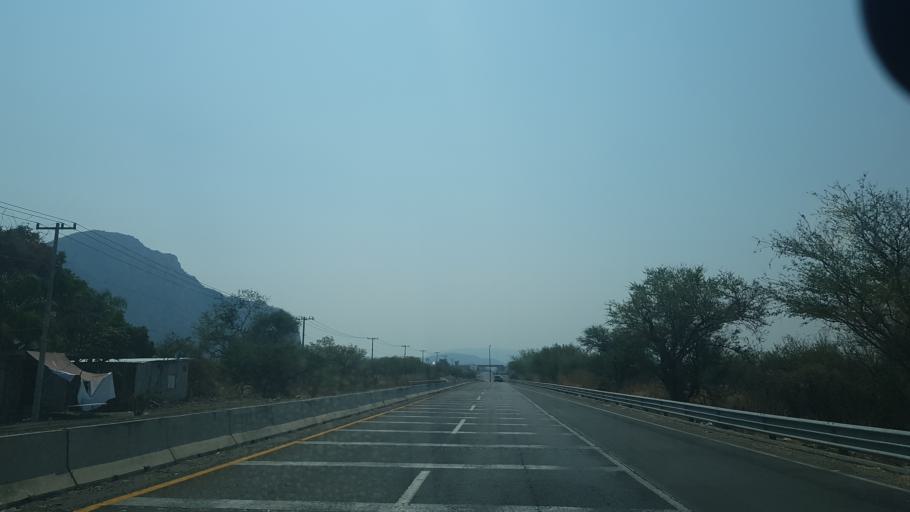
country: MX
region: Morelos
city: Jantetelco
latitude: 18.7077
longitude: -98.7763
